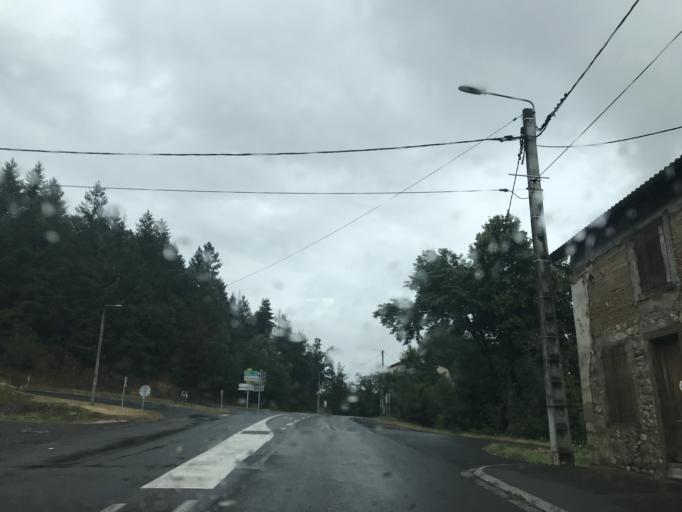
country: FR
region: Auvergne
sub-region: Departement du Puy-de-Dome
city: Ambert
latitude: 45.5471
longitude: 3.7289
